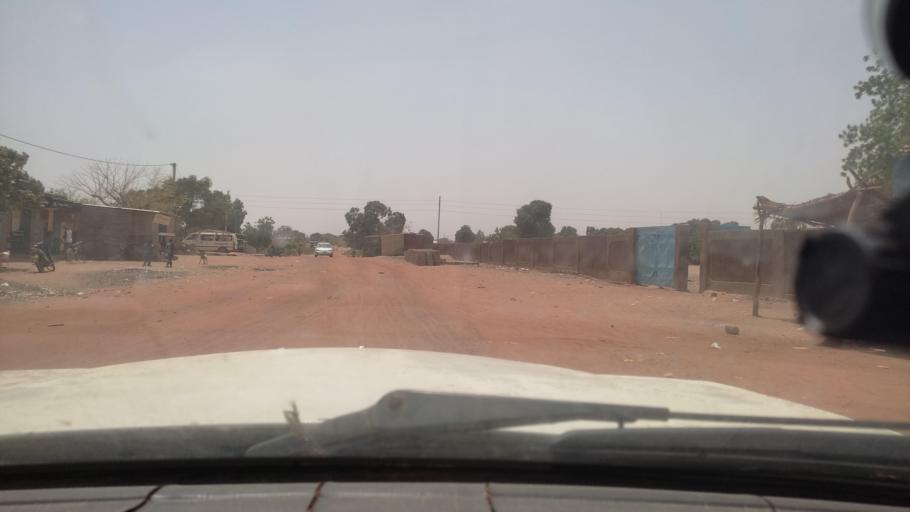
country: BF
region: Est
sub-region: Province du Gourma
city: Fada N'gourma
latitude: 12.0727
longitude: 0.3612
